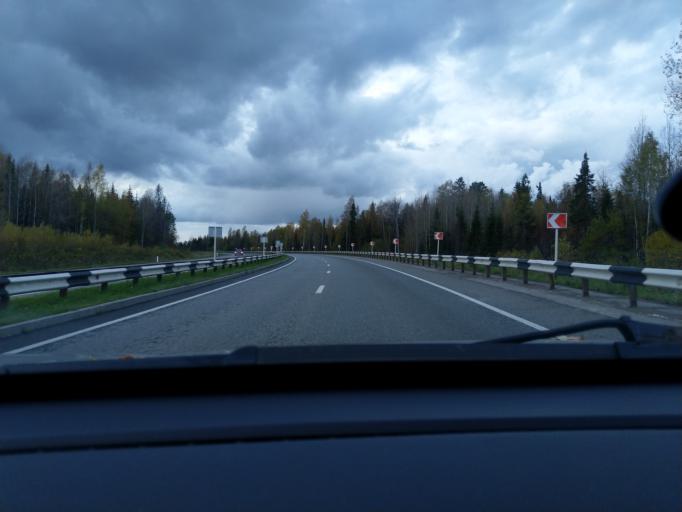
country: RU
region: Perm
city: Polazna
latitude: 58.3372
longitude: 56.4776
